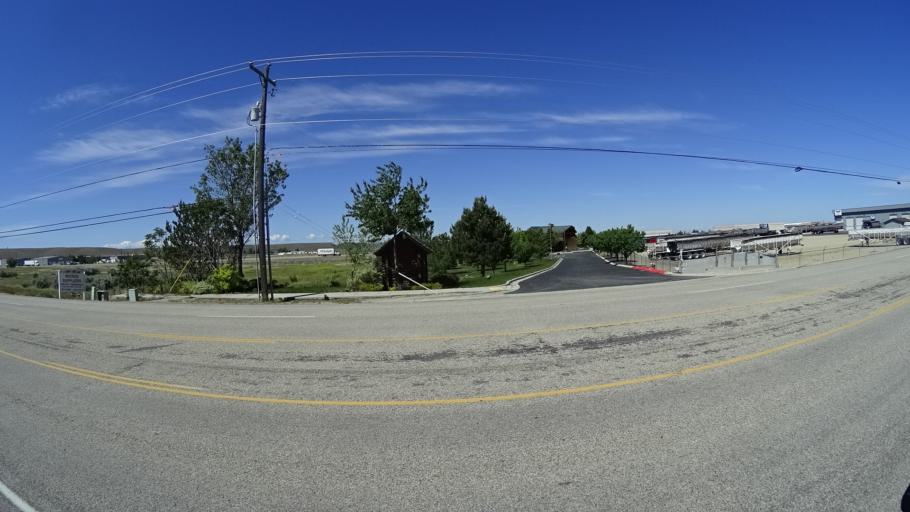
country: US
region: Idaho
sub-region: Ada County
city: Boise
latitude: 43.5313
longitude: -116.1513
